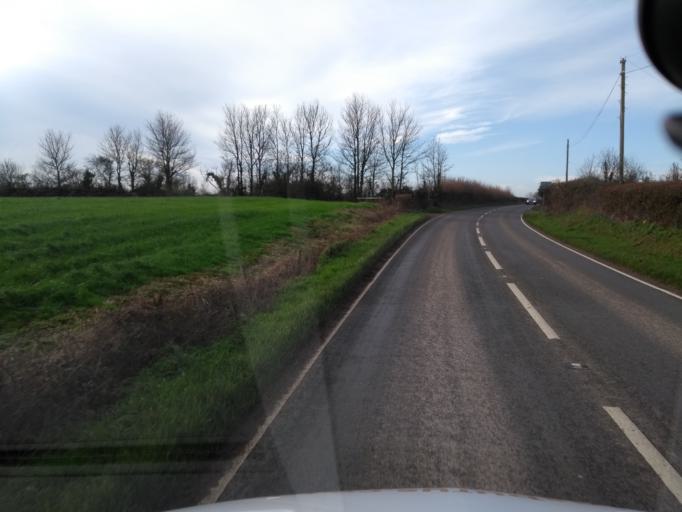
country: GB
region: England
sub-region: Somerset
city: Westonzoyland
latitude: 51.0544
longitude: -2.9559
